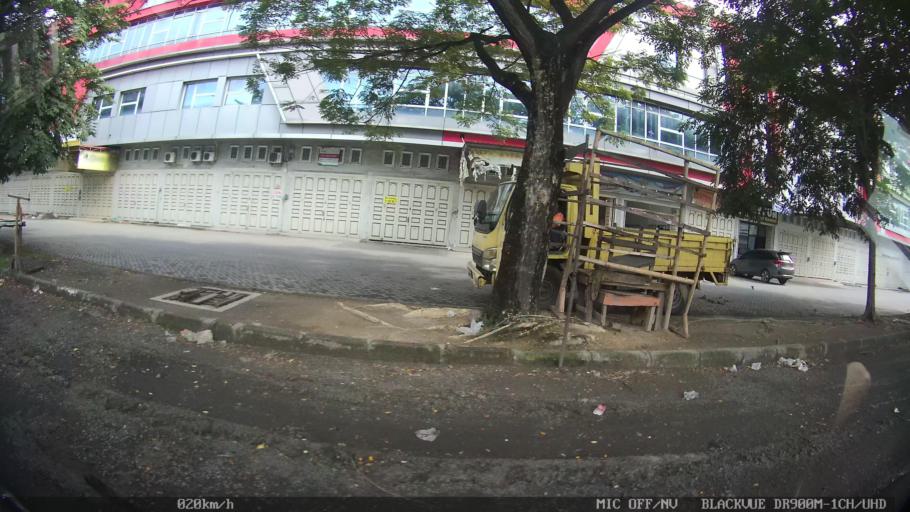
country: ID
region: North Sumatra
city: Medan
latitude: 3.6305
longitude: 98.6979
